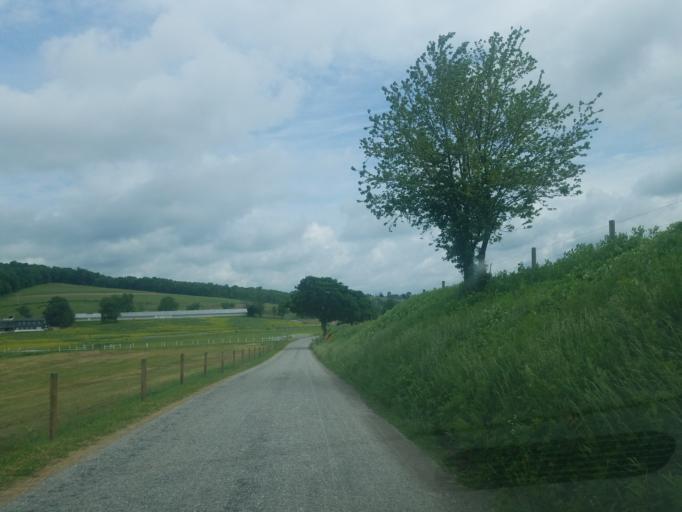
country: US
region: Ohio
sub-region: Tuscarawas County
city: Sugarcreek
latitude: 40.5206
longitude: -81.7519
